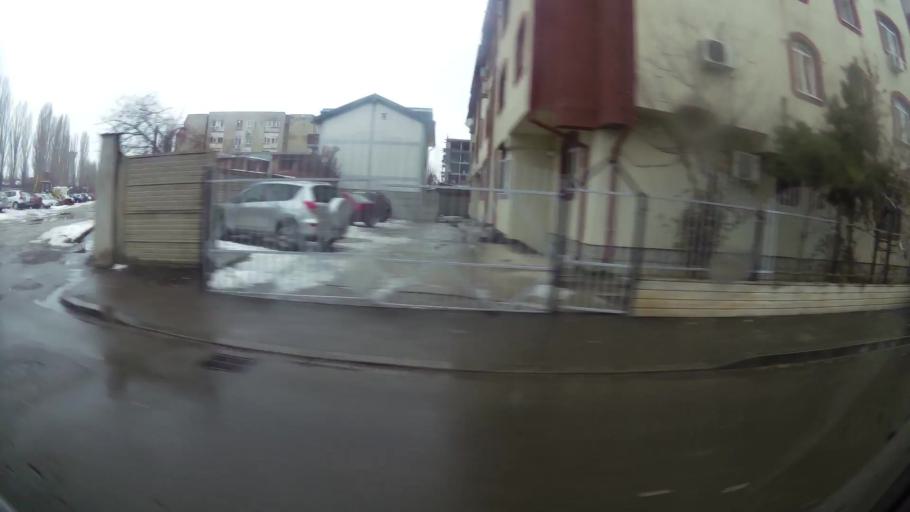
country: RO
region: Ilfov
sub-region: Comuna Chiajna
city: Rosu
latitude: 44.4294
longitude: 26.0121
